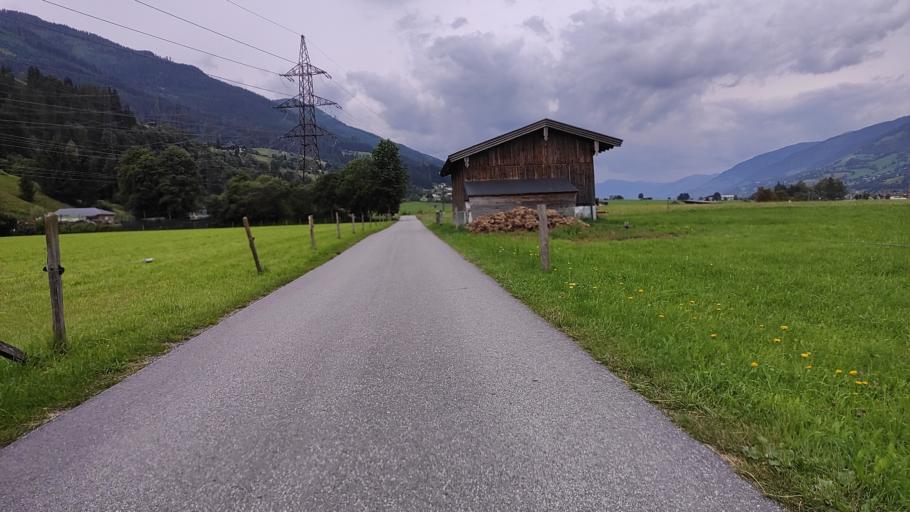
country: AT
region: Salzburg
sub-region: Politischer Bezirk Zell am See
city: Niedernsill
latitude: 47.2768
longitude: 12.6738
